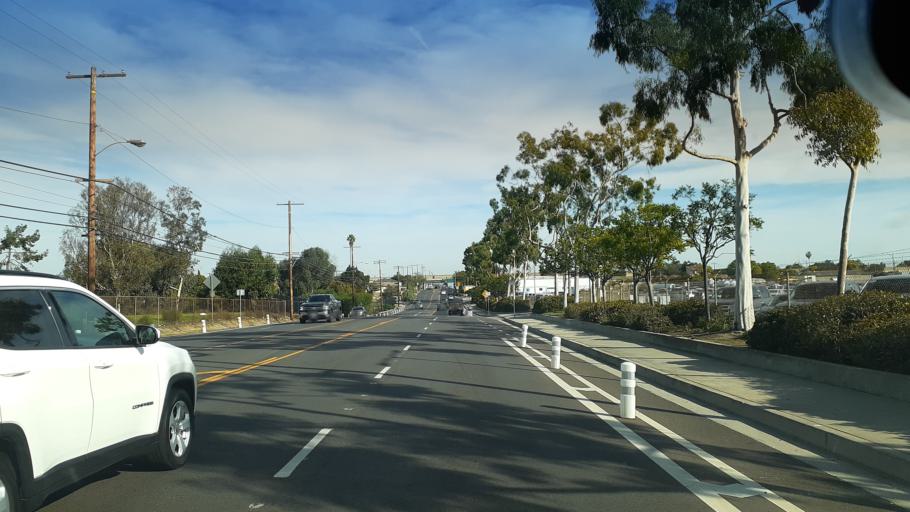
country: US
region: California
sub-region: Los Angeles County
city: Lomita
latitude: 33.7787
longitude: -118.2854
